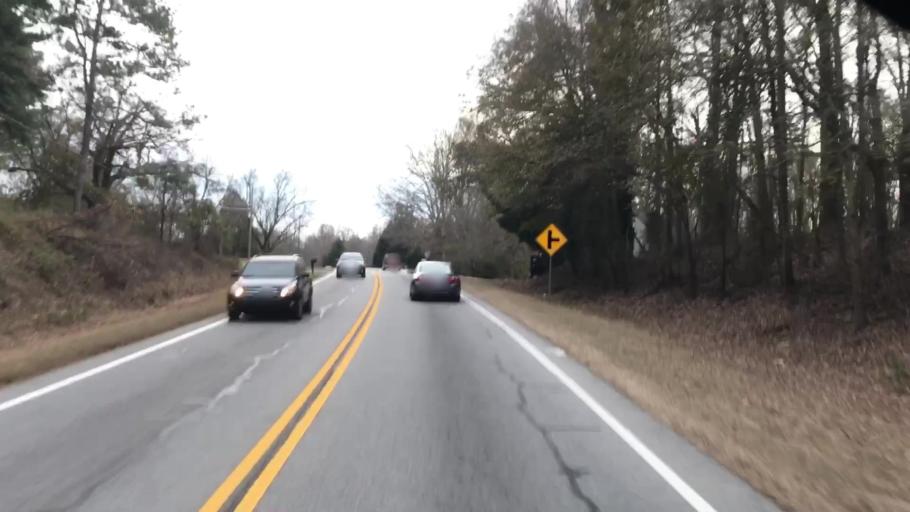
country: US
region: Georgia
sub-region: Barrow County
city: Auburn
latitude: 34.0300
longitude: -83.7742
